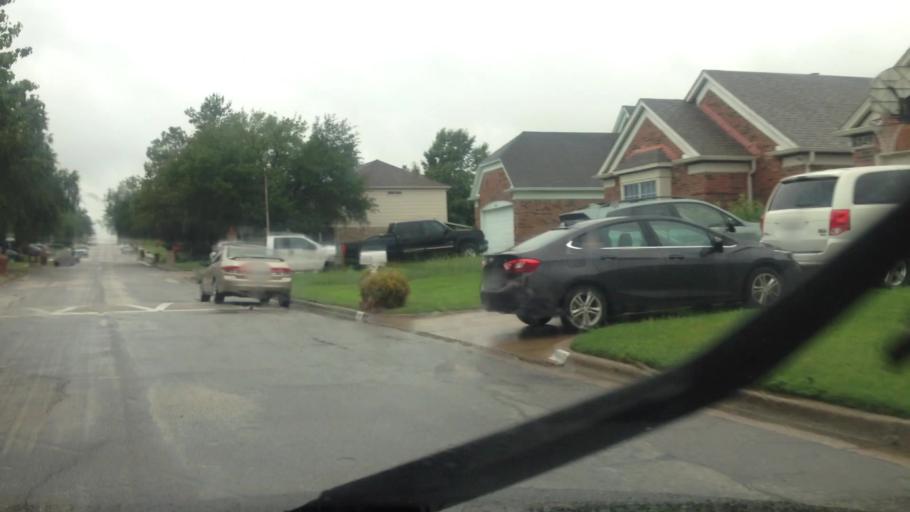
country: US
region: Texas
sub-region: Tarrant County
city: Watauga
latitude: 32.8863
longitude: -97.2312
